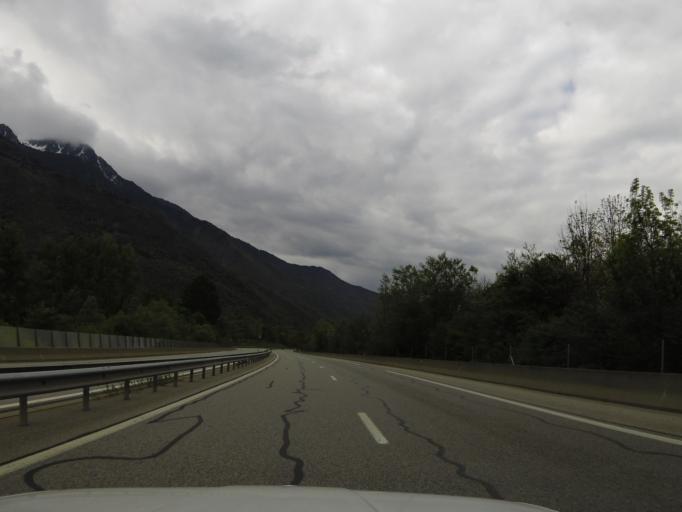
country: FR
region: Rhone-Alpes
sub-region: Departement de la Savoie
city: Saint-Remy-de-Maurienne
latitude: 45.3952
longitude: 6.2741
